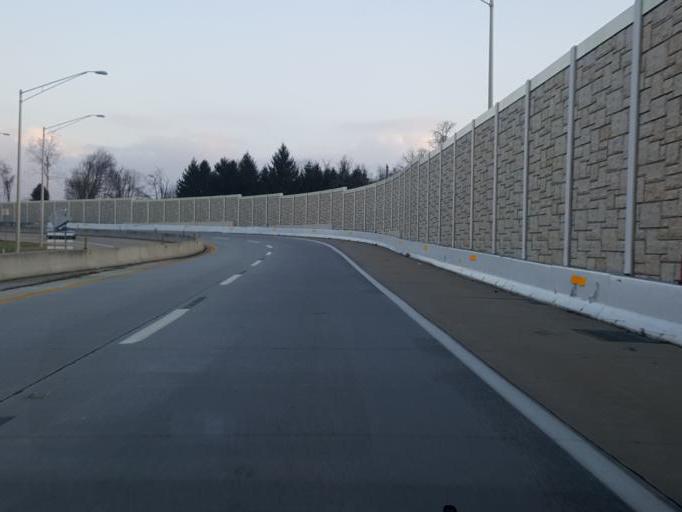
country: US
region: Pennsylvania
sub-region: Dauphin County
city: Highspire
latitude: 40.2139
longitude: -76.7882
